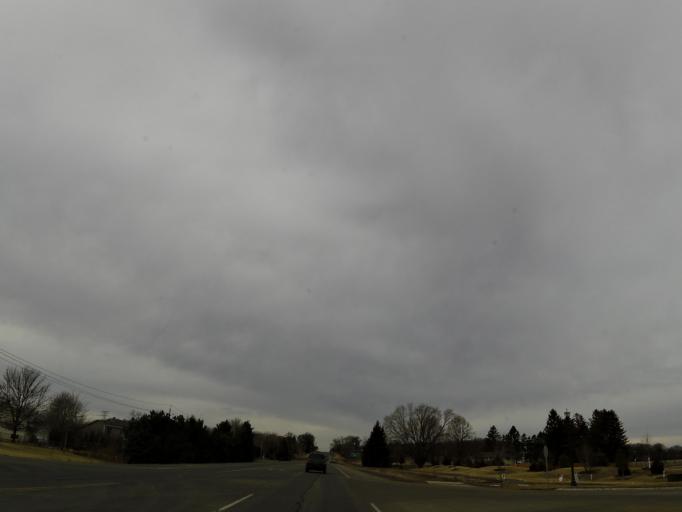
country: US
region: Minnesota
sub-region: Washington County
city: Cottage Grove
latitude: 44.8481
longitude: -92.9163
